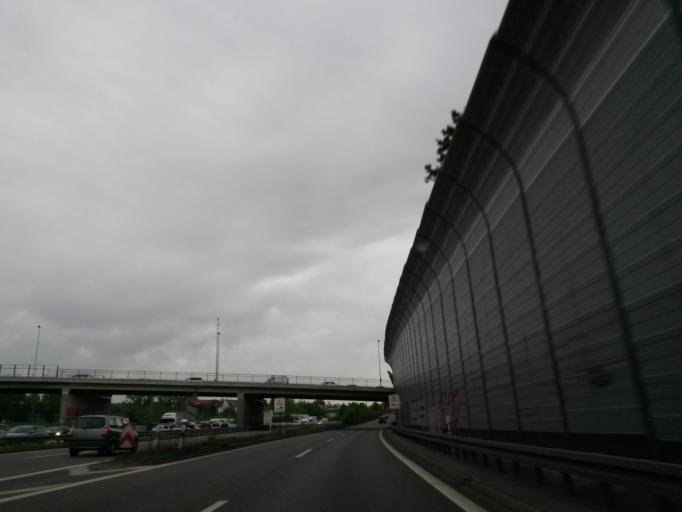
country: DE
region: Baden-Wuerttemberg
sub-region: Regierungsbezirk Stuttgart
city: Stuttgart Feuerbach
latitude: 48.8356
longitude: 9.1670
